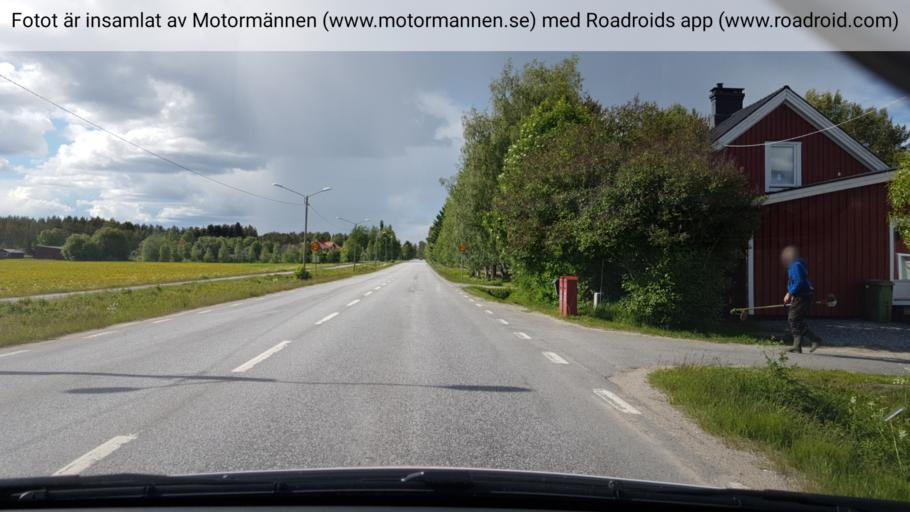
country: SE
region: Vaesterbotten
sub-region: Umea Kommun
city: Roback
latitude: 63.9394
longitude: 20.1602
